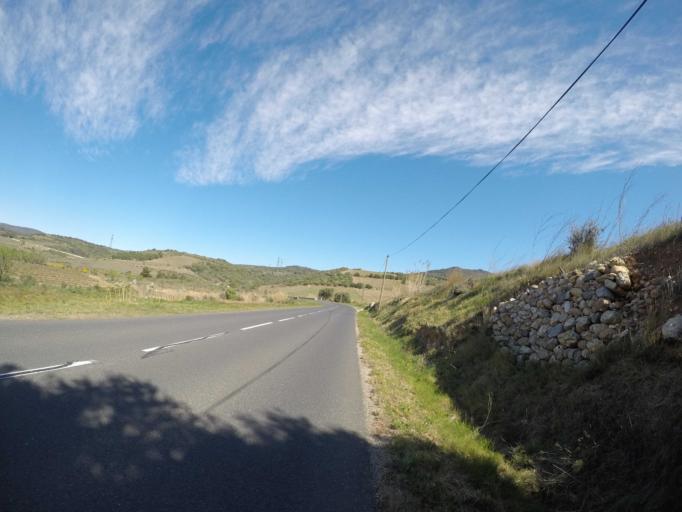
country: FR
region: Languedoc-Roussillon
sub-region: Departement des Pyrenees-Orientales
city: Millas
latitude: 42.7113
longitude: 2.6836
